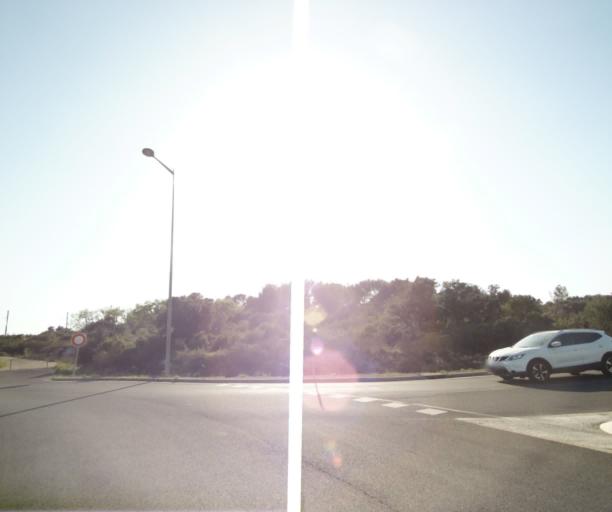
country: FR
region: Languedoc-Roussillon
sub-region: Departement de l'Herault
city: Le Cres
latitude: 43.6488
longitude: 3.9283
